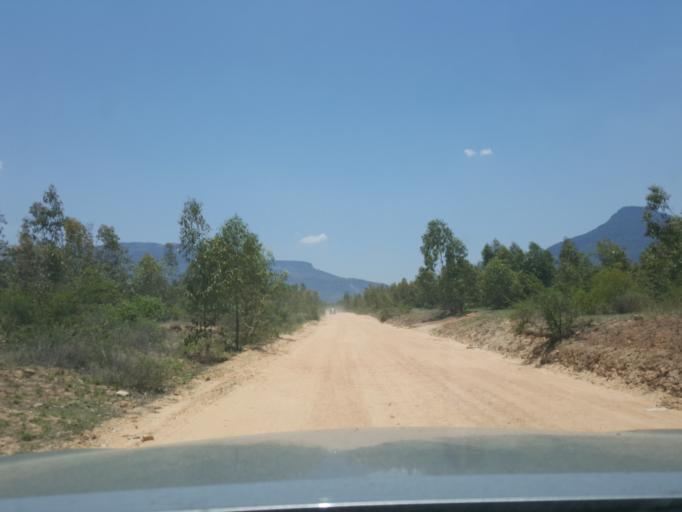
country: ZA
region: Limpopo
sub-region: Mopani District Municipality
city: Hoedspruit
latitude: -24.5868
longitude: 30.9696
